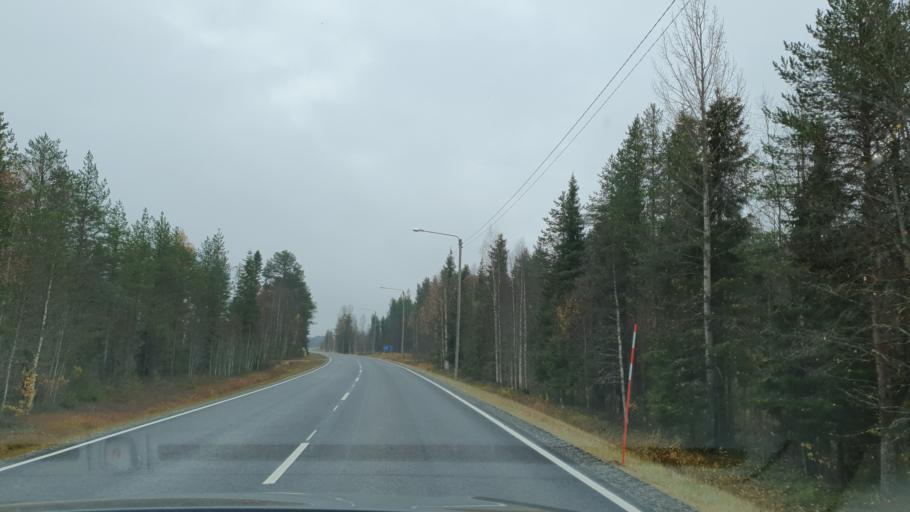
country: FI
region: Lapland
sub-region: Rovaniemi
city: Ranua
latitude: 66.1058
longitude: 26.3262
